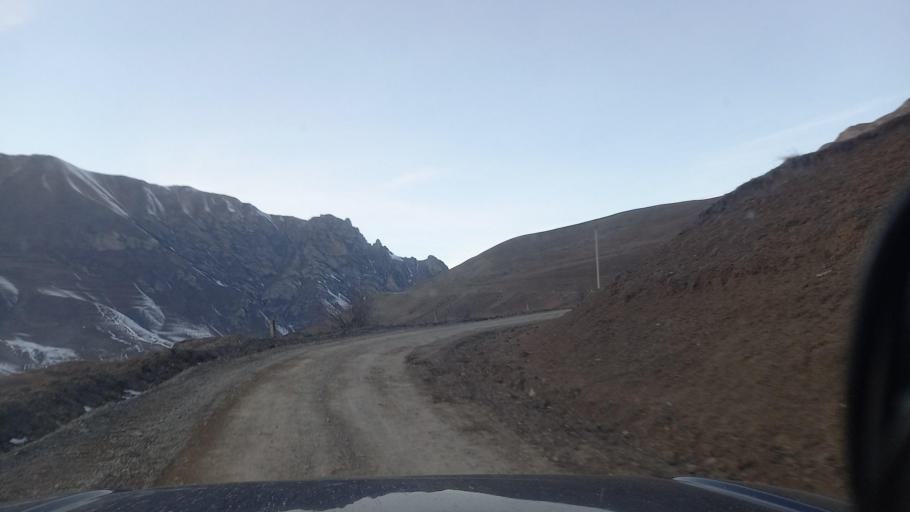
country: RU
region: Ingushetiya
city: Dzhayrakh
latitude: 42.8376
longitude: 44.5427
